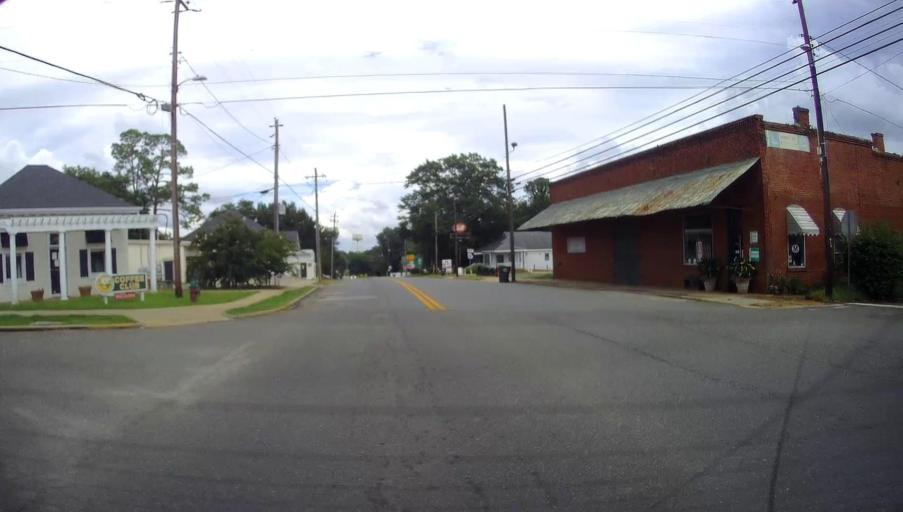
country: US
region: Georgia
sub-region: Marion County
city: Buena Vista
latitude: 32.3180
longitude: -84.5169
